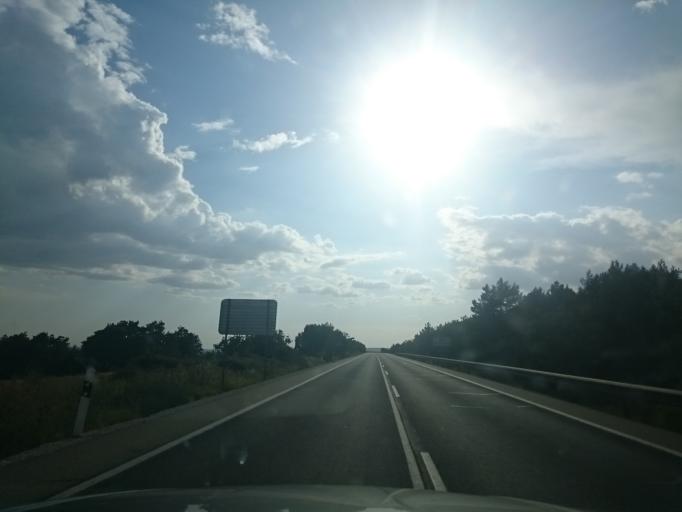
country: ES
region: Castille and Leon
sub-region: Provincia de Burgos
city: Arlanzon
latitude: 42.3508
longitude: -3.4270
